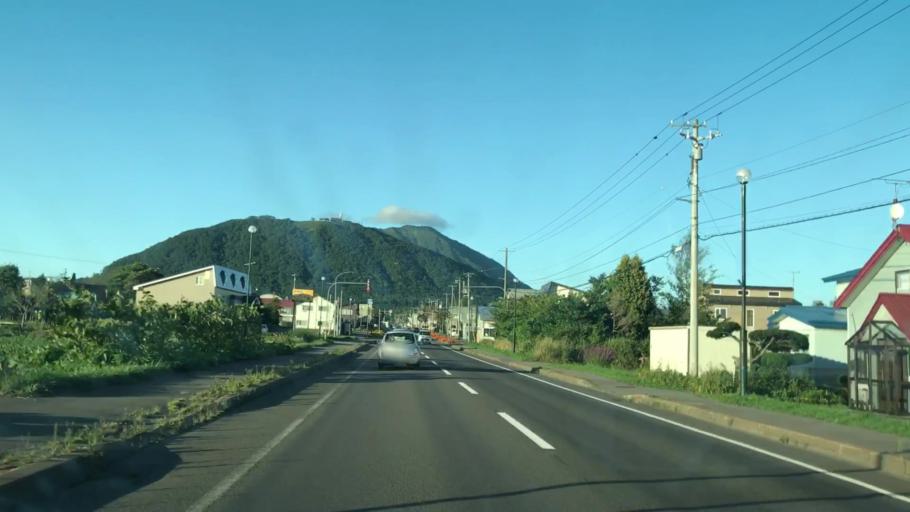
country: JP
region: Hokkaido
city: Niseko Town
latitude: 42.7315
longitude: 140.8714
